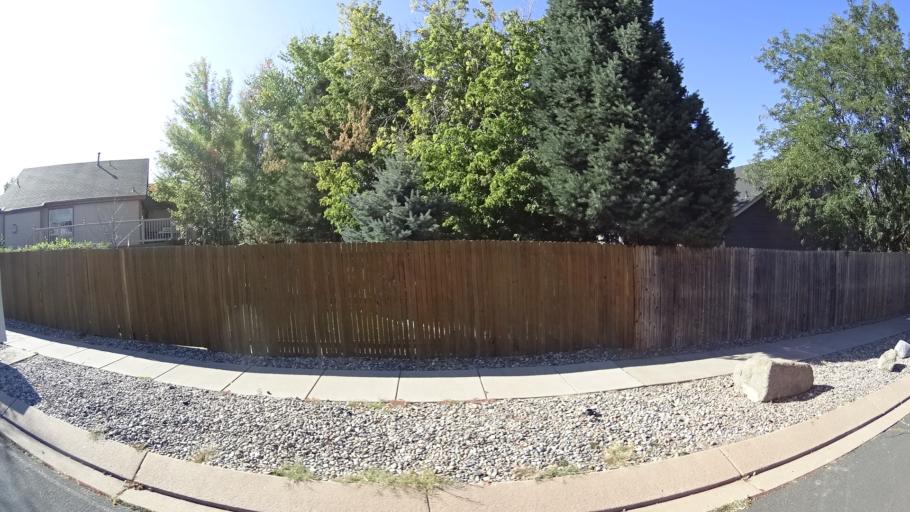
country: US
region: Colorado
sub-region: El Paso County
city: Cimarron Hills
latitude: 38.8808
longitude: -104.7053
